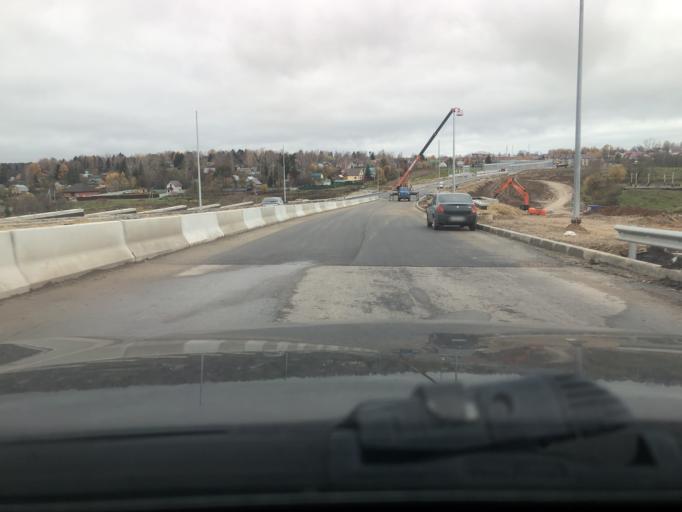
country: RU
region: Moskovskaya
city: Sergiyev Posad
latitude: 56.2987
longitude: 38.1007
